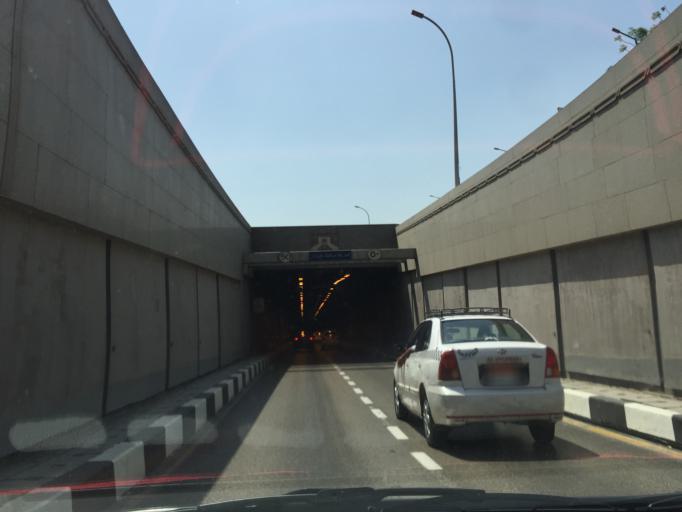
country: EG
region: Muhafazat al Qahirah
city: Cairo
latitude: 30.0462
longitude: 31.2716
